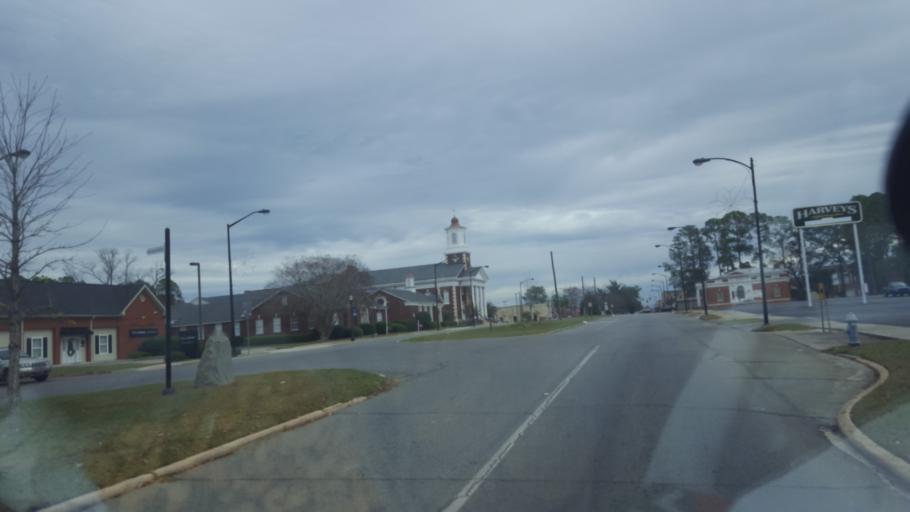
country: US
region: Georgia
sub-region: Ben Hill County
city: Fitzgerald
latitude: 31.7147
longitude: -83.2575
